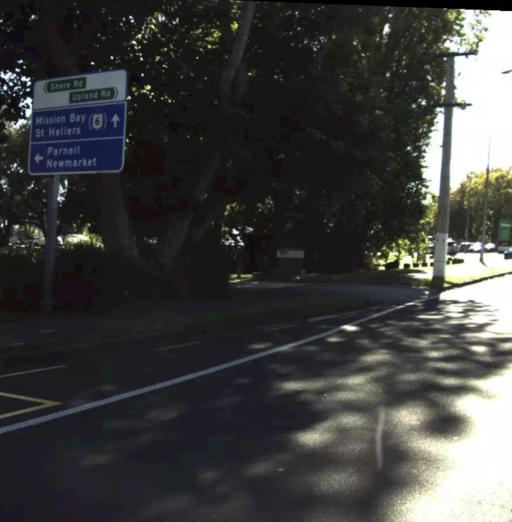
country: NZ
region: Auckland
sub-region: Auckland
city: Auckland
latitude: -36.8675
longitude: 174.8065
